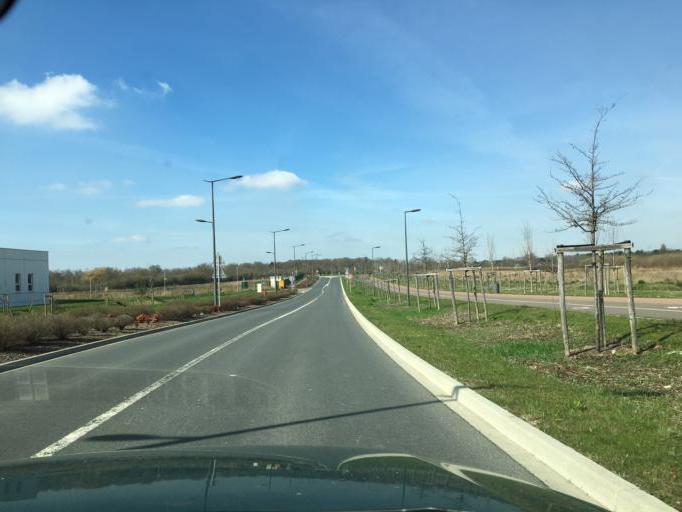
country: FR
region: Centre
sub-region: Departement du Loiret
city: Saran
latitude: 47.9408
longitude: 1.8797
